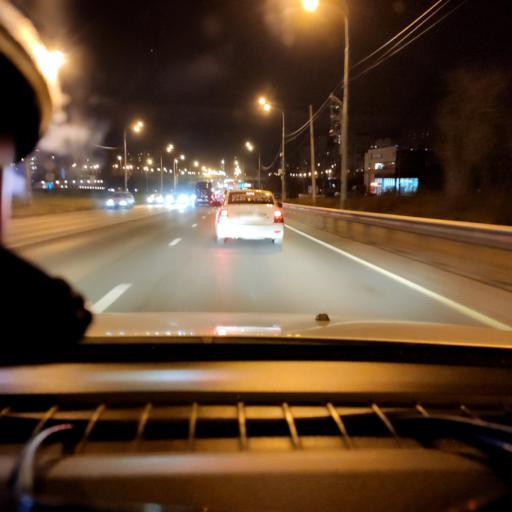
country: RU
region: Samara
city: Samara
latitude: 53.2717
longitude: 50.2241
